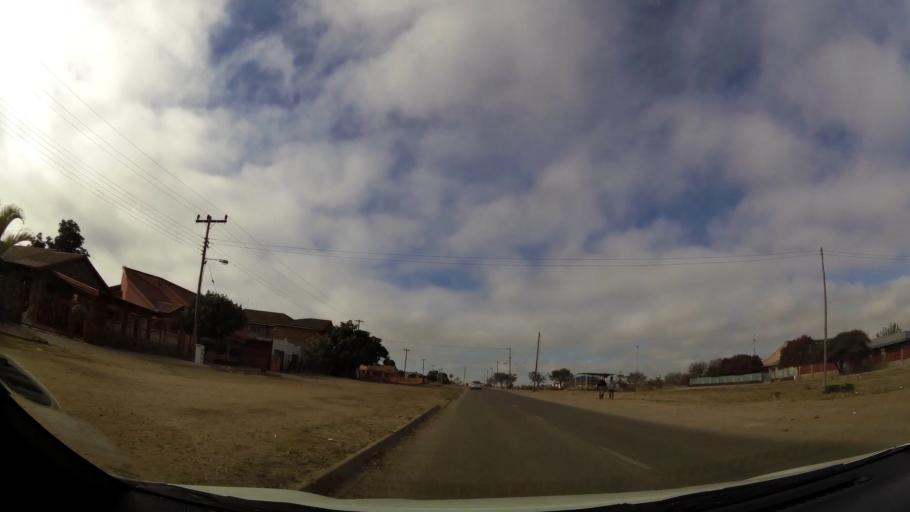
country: ZA
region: Limpopo
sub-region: Capricorn District Municipality
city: Polokwane
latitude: -23.8483
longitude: 29.3817
